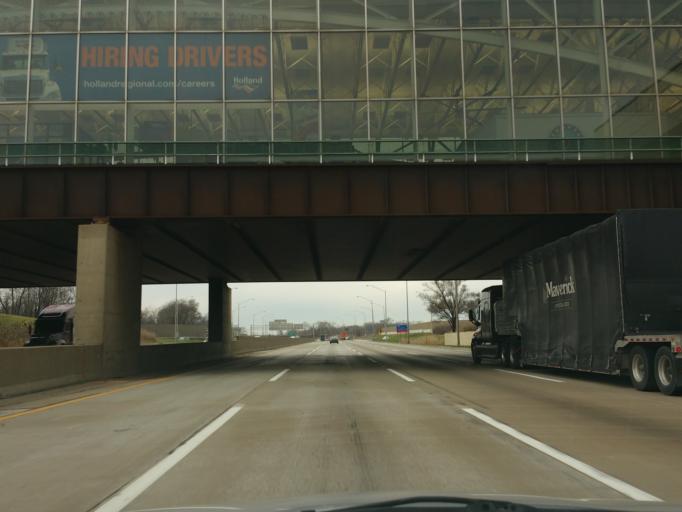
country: US
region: Illinois
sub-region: Cook County
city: Thornton
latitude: 41.5787
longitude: -87.5988
